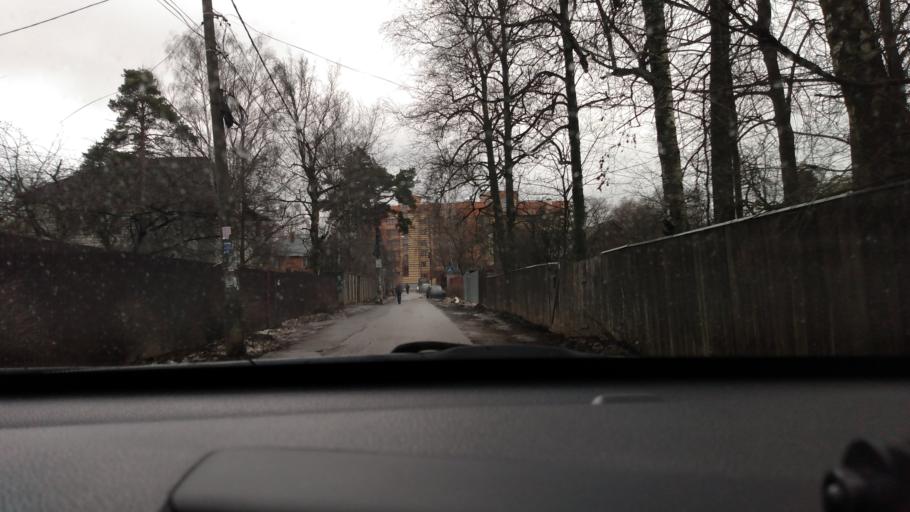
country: RU
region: Moskovskaya
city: Druzhba
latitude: 55.8979
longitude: 37.7431
